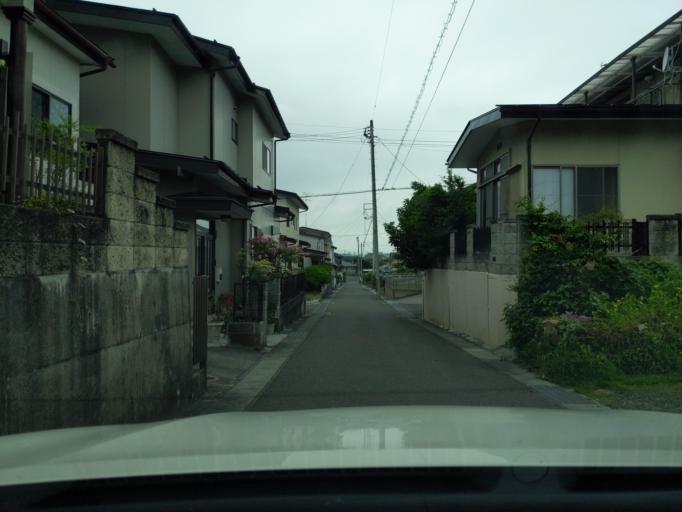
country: JP
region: Fukushima
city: Koriyama
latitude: 37.3987
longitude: 140.4173
